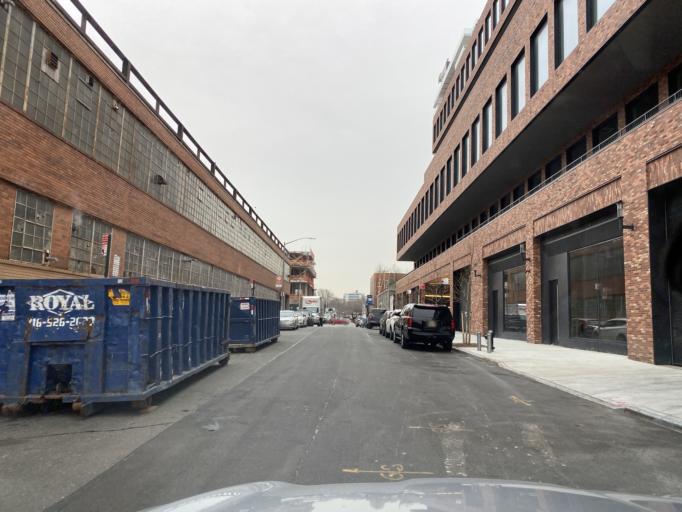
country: US
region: New York
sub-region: Queens County
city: Long Island City
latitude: 40.7226
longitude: -73.9580
